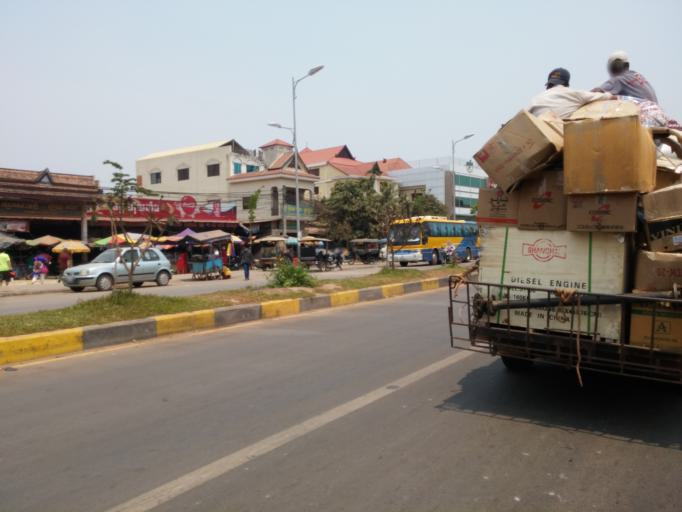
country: KH
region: Siem Reap
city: Siem Reap
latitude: 13.3608
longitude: 103.8678
